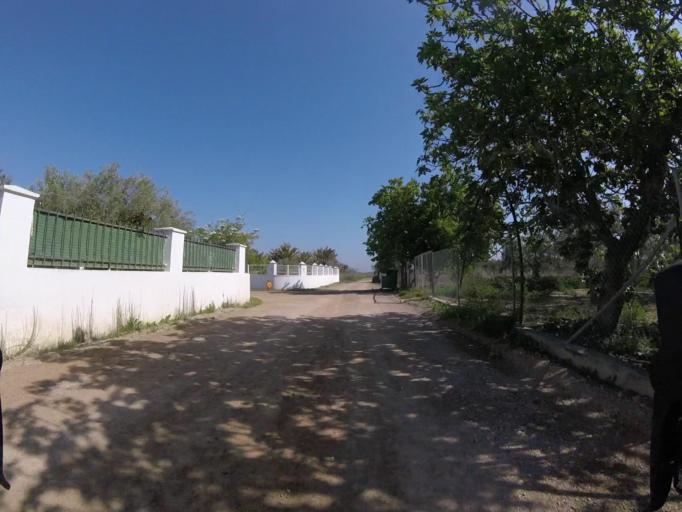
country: ES
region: Valencia
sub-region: Provincia de Castello
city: Orpesa/Oropesa del Mar
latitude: 40.1490
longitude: 0.1659
